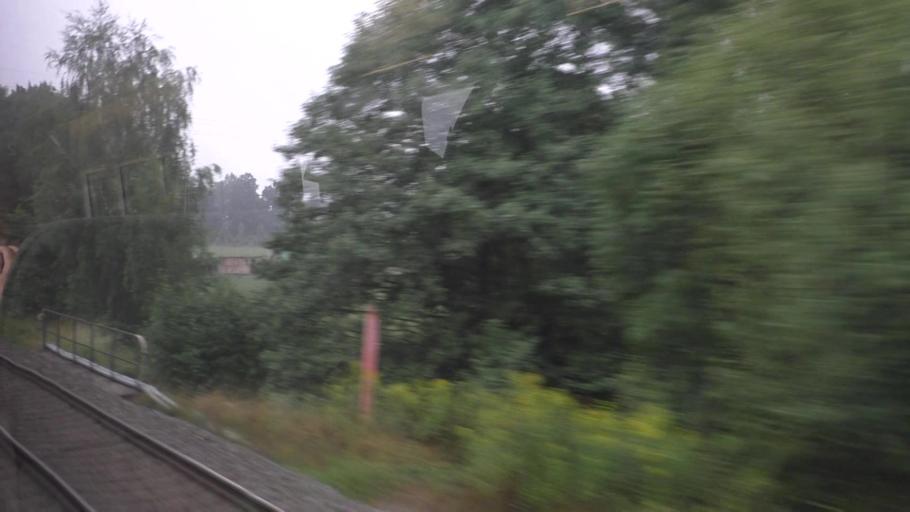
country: DE
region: Saxony
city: Arnsdorf
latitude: 51.0960
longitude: 13.9726
